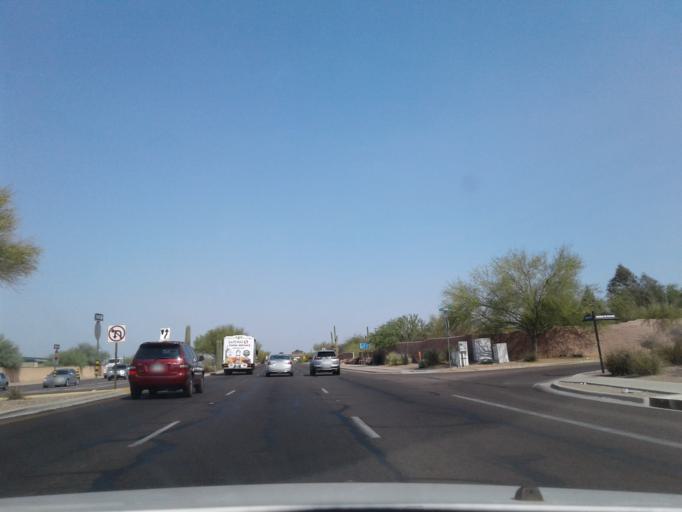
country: US
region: Arizona
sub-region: Pima County
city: Catalina Foothills
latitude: 32.3236
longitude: -110.9332
